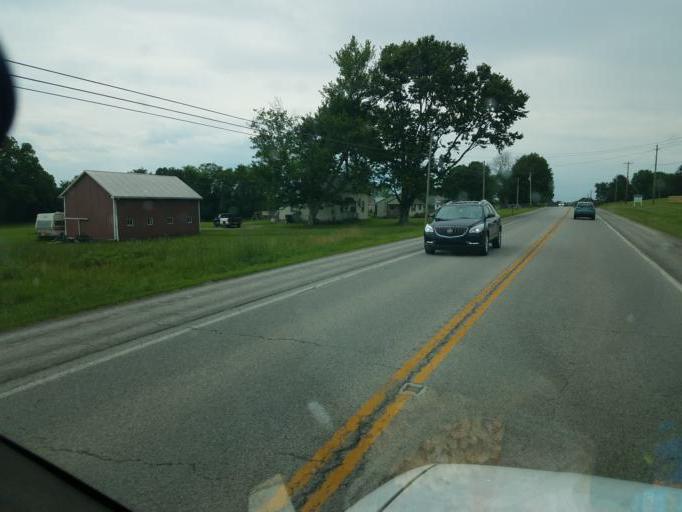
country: US
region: Ohio
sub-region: Wayne County
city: Apple Creek
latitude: 40.7311
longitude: -81.8023
